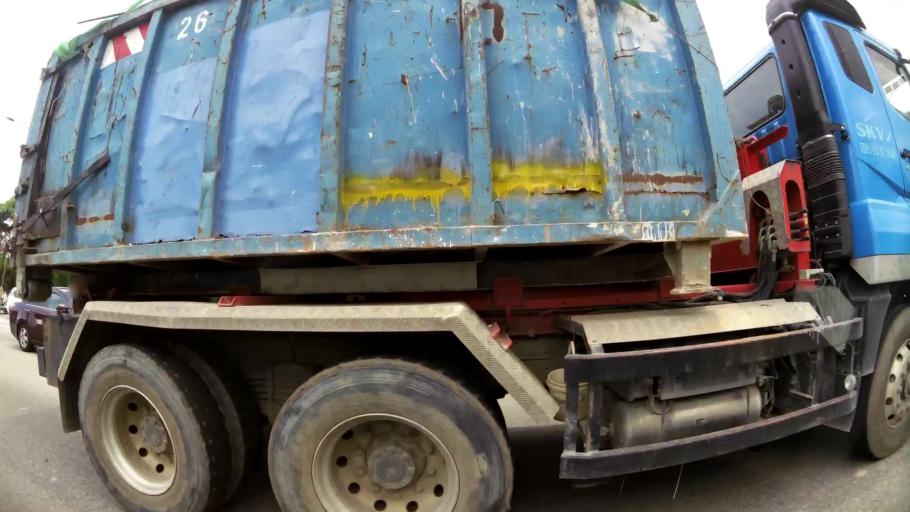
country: SG
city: Singapore
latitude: 1.3522
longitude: 103.8574
